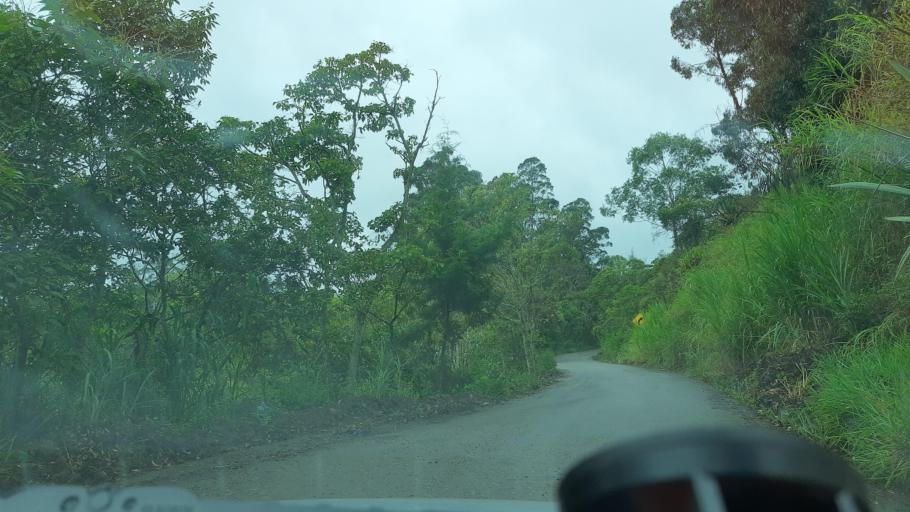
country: CO
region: Cundinamarca
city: Manta
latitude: 5.0466
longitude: -73.5105
